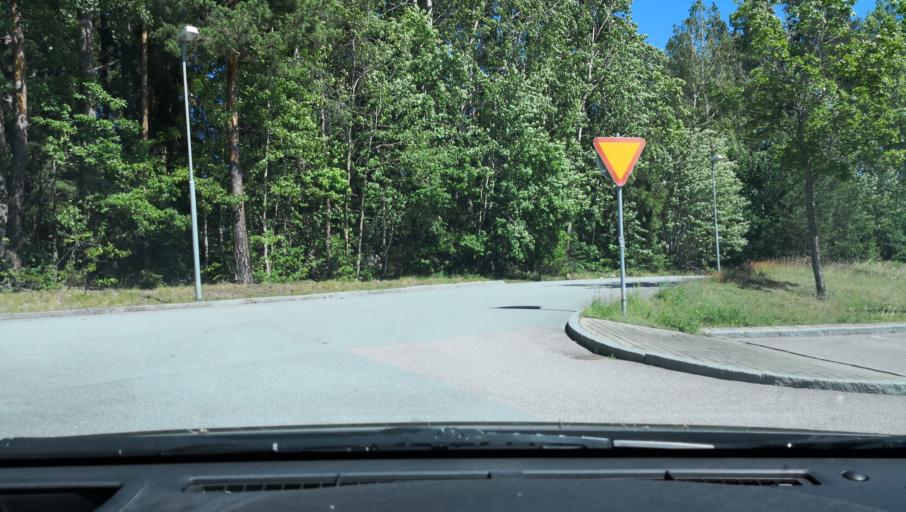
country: SE
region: Vaestmanland
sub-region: Kungsors Kommun
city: Kungsoer
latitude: 59.2820
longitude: 16.1105
